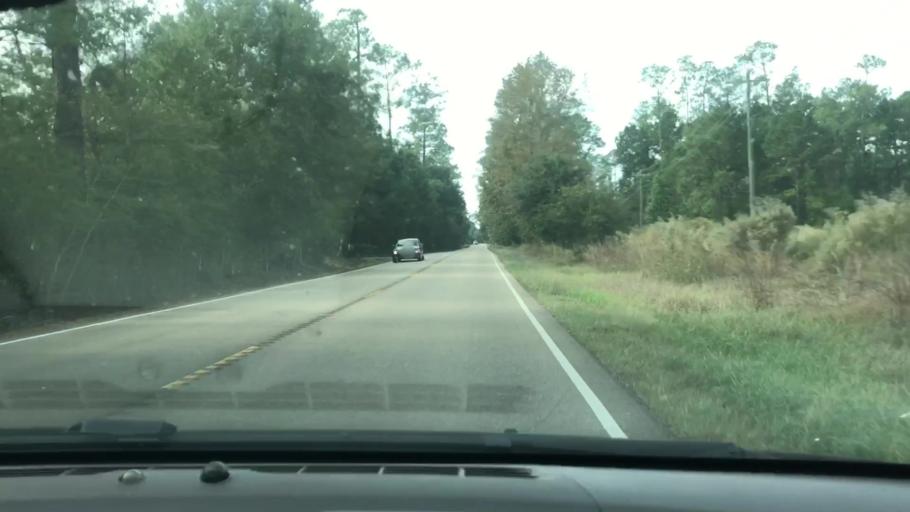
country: US
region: Louisiana
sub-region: Saint Tammany Parish
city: Abita Springs
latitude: 30.4991
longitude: -89.9983
